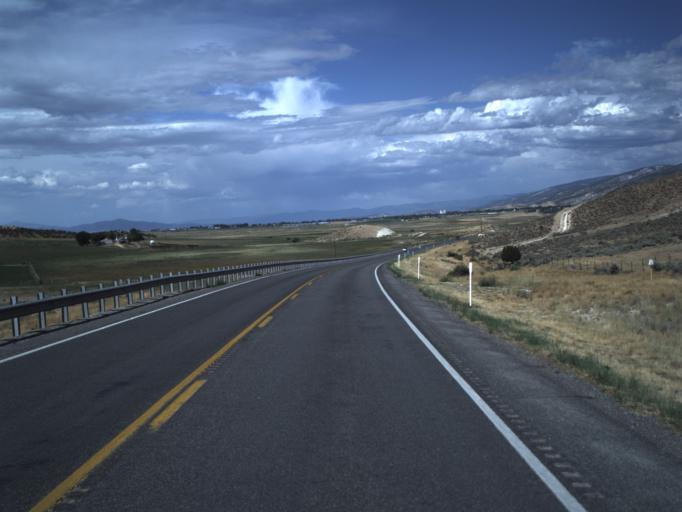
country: US
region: Utah
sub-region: Sanpete County
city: Manti
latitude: 39.2132
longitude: -111.6878
